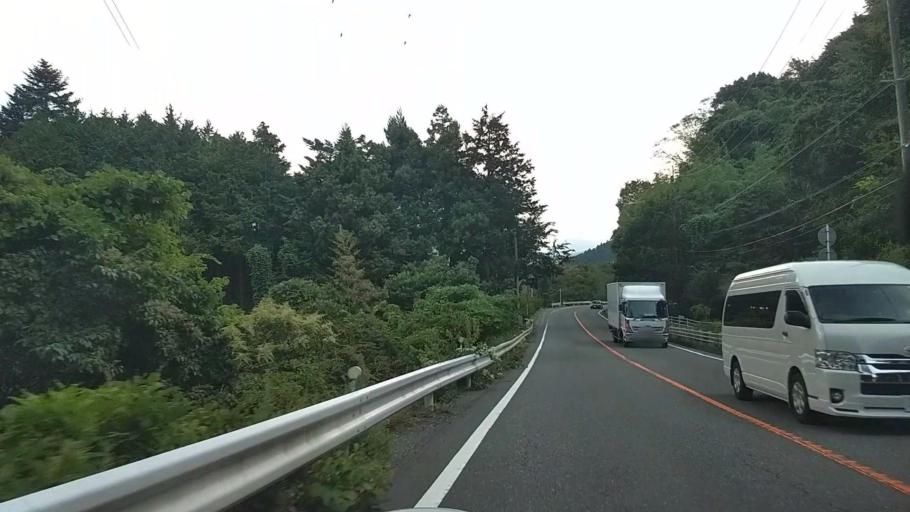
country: JP
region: Shizuoka
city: Fujinomiya
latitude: 35.3214
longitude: 138.4391
